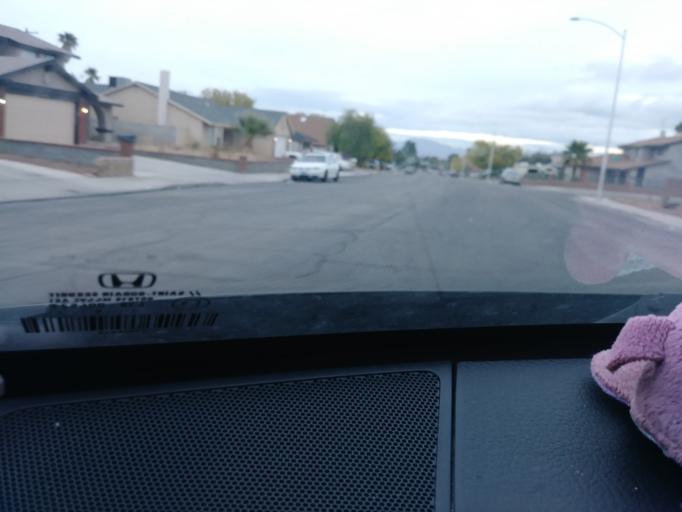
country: US
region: Nevada
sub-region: Clark County
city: Spring Valley
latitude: 36.1770
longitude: -115.2149
